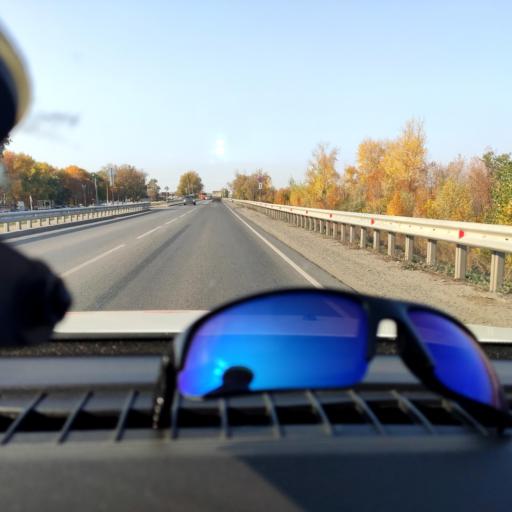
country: RU
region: Samara
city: Samara
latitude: 53.1149
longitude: 50.1258
